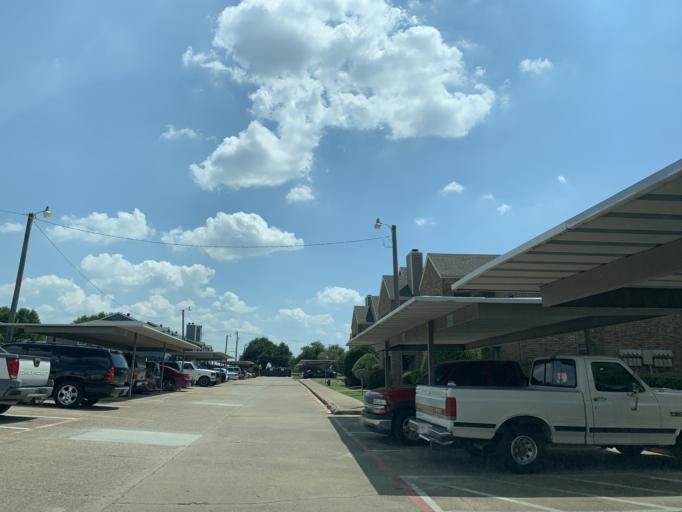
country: US
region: Texas
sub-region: Tarrant County
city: Watauga
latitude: 32.8355
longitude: -97.2686
